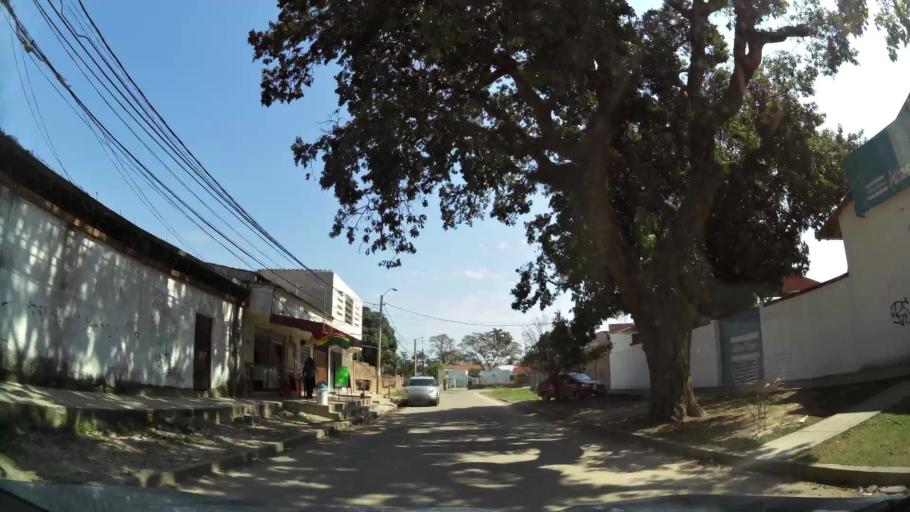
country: BO
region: Santa Cruz
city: Santa Cruz de la Sierra
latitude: -17.7482
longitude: -63.1806
